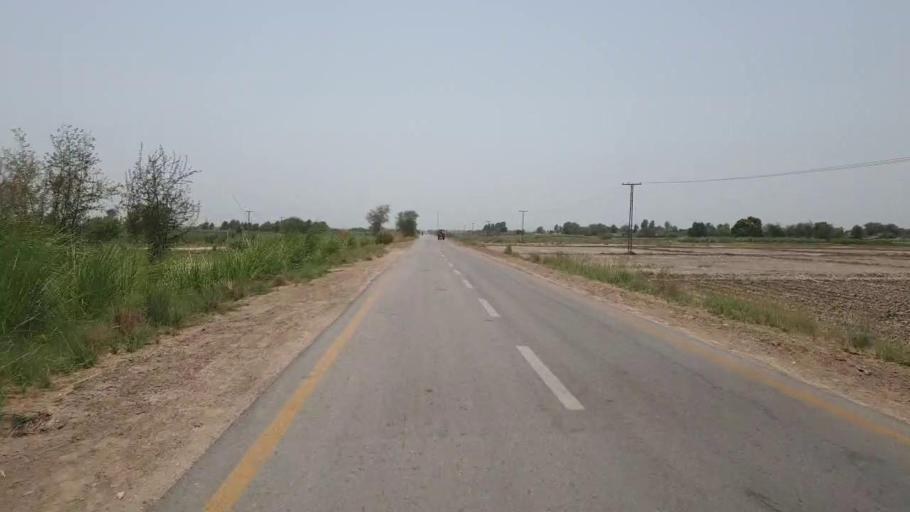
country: PK
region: Sindh
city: Moro
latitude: 26.6004
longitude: 68.0833
